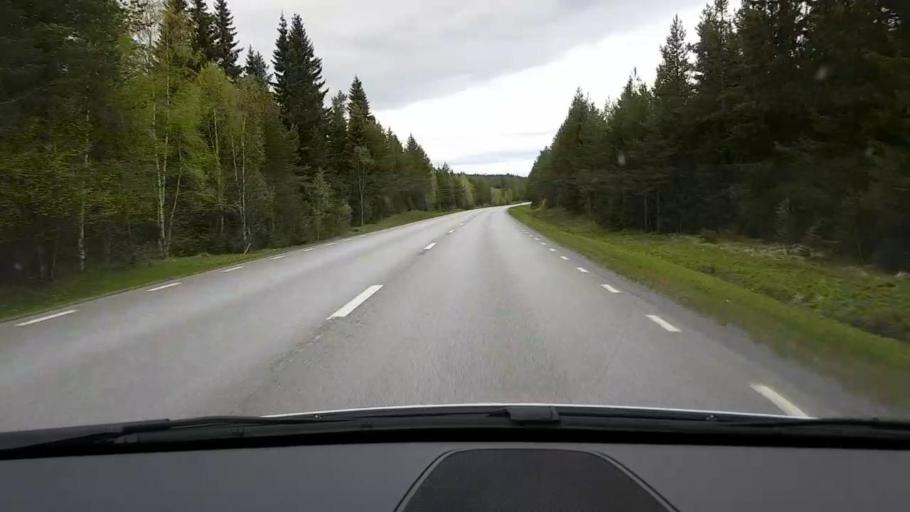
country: SE
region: Jaemtland
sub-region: Krokoms Kommun
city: Valla
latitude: 63.2876
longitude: 13.9282
